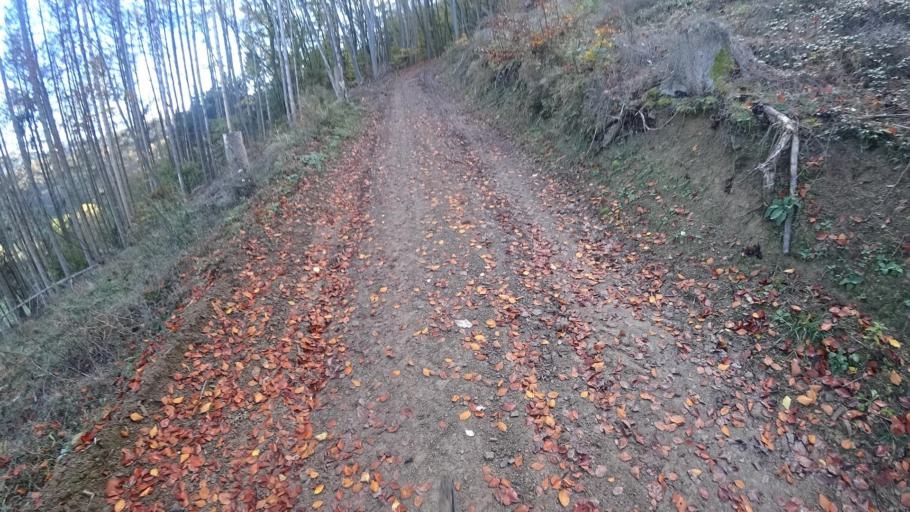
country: DE
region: Rheinland-Pfalz
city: Kirchsahr
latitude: 50.5075
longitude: 6.9132
